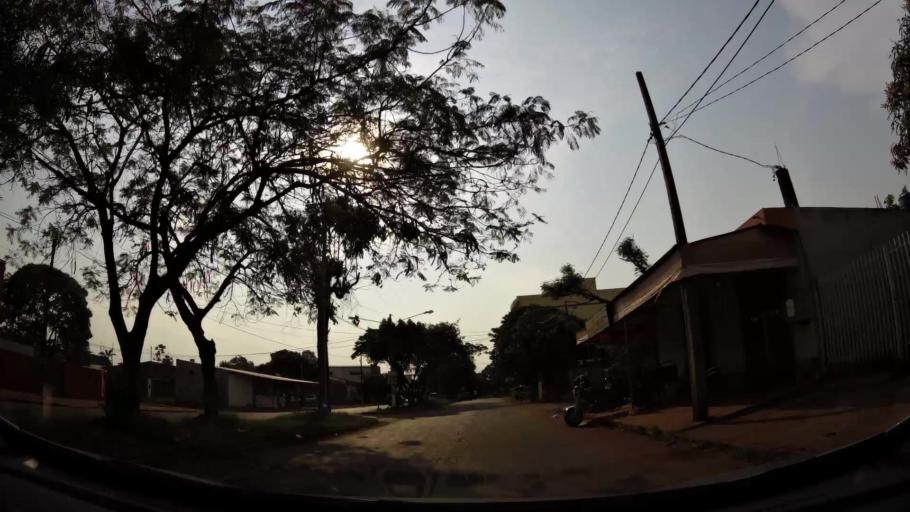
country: PY
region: Alto Parana
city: Ciudad del Este
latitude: -25.4853
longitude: -54.6622
